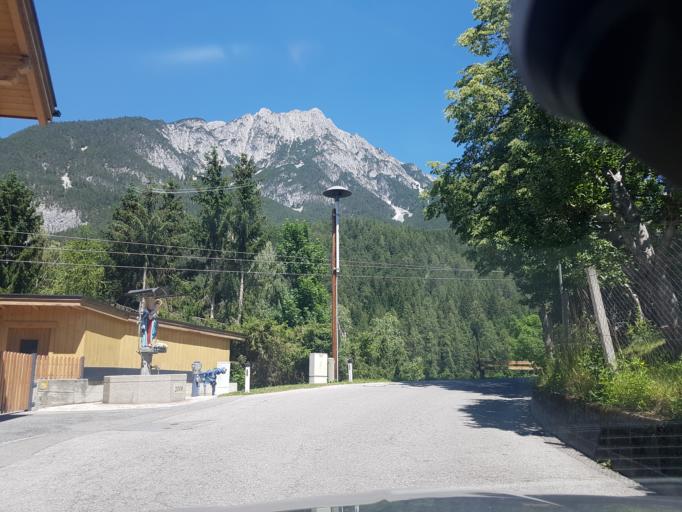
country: AT
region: Tyrol
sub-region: Politischer Bezirk Imst
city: Nassereith
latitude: 47.3090
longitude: 10.8522
